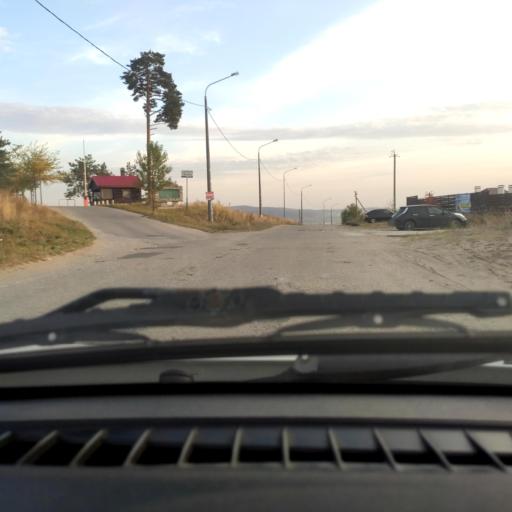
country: RU
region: Samara
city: Zhigulevsk
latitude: 53.4846
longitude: 49.5385
